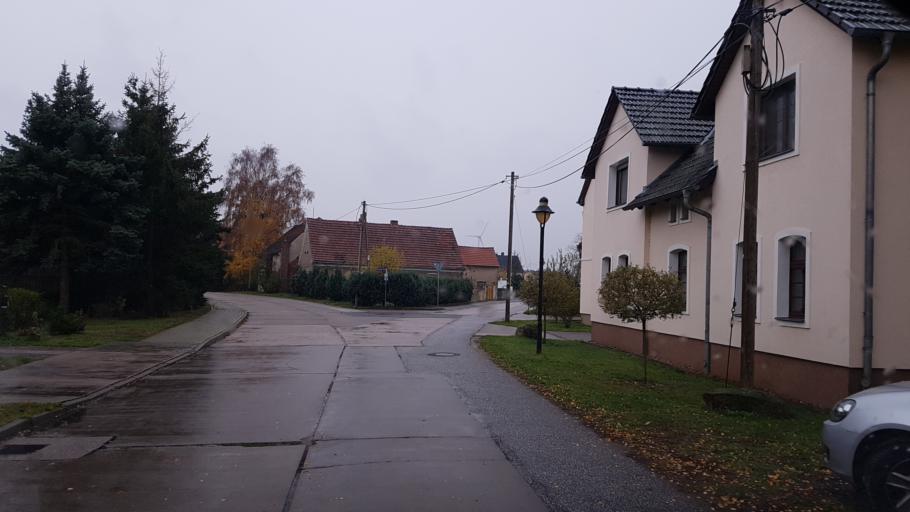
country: DE
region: Brandenburg
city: Herzberg
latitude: 51.6531
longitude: 13.2226
